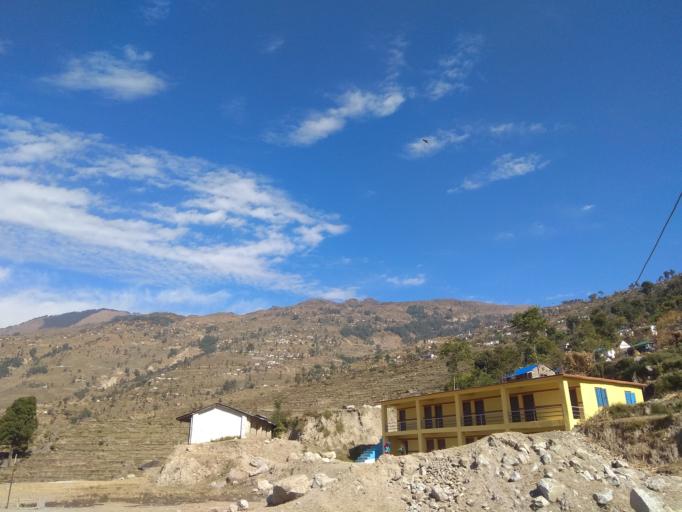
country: NP
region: Far Western
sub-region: Seti Zone
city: Achham
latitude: 29.2393
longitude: 81.6331
